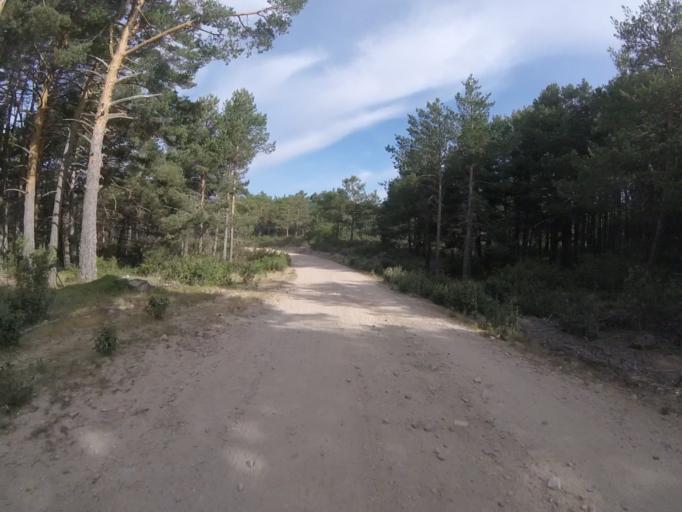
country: ES
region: Castille and Leon
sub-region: Provincia de Avila
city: Peguerinos
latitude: 40.6537
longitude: -4.1823
